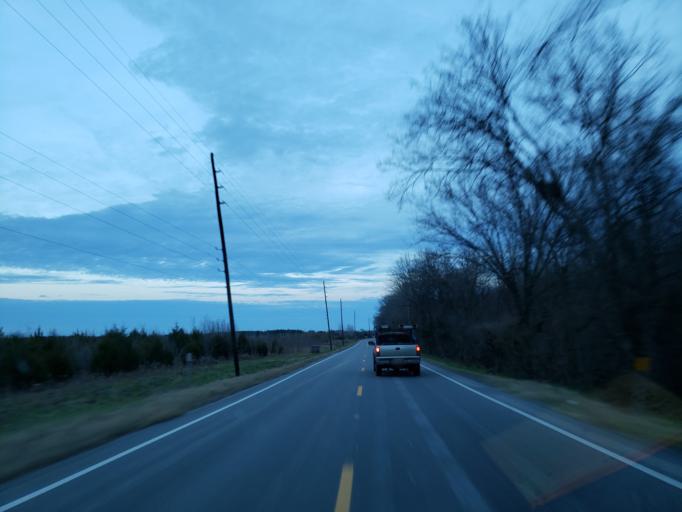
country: US
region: Alabama
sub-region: Sumter County
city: Livingston
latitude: 32.8082
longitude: -88.2914
